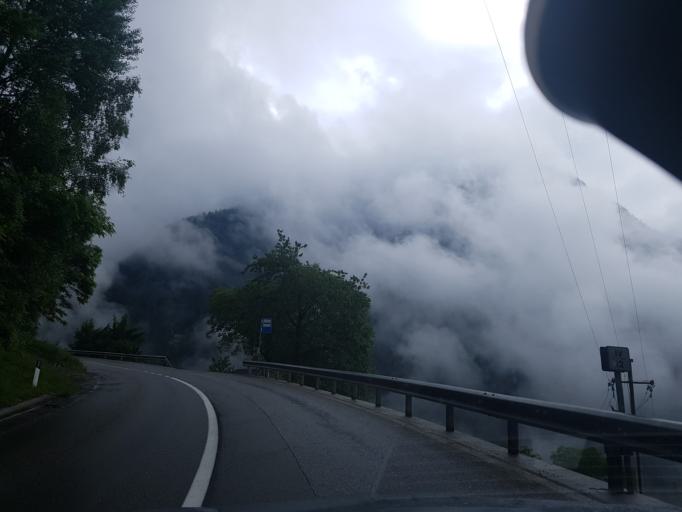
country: IT
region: Trentino-Alto Adige
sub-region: Bolzano
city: Laion
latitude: 46.5993
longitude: 11.6069
